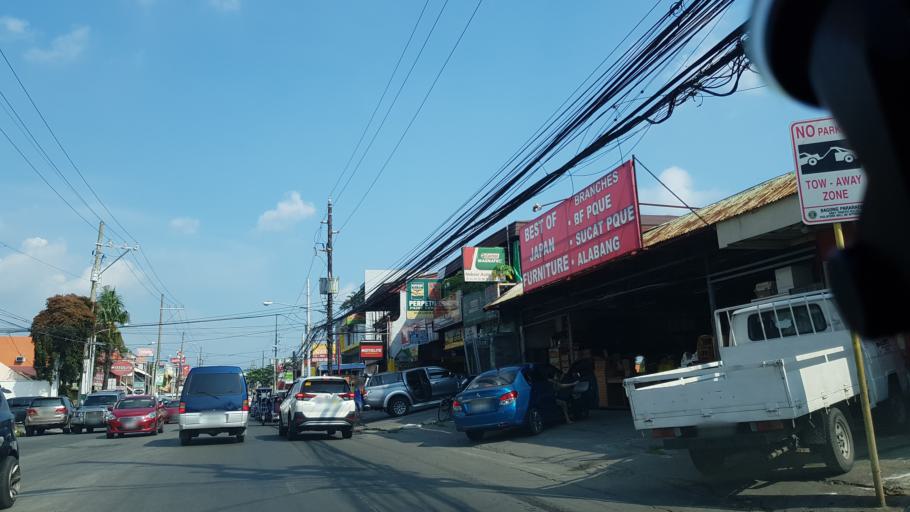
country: PH
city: Sambayanihan People's Village
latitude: 14.4837
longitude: 121.0333
